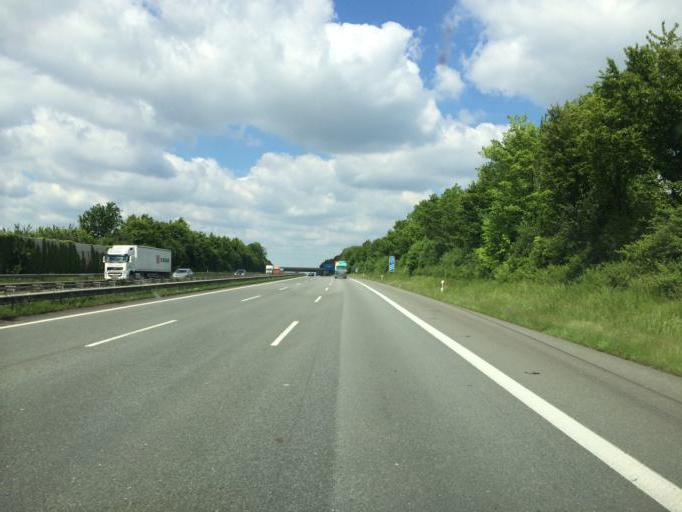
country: DE
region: North Rhine-Westphalia
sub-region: Regierungsbezirk Detmold
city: Leopoldshohe
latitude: 52.0531
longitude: 8.6574
